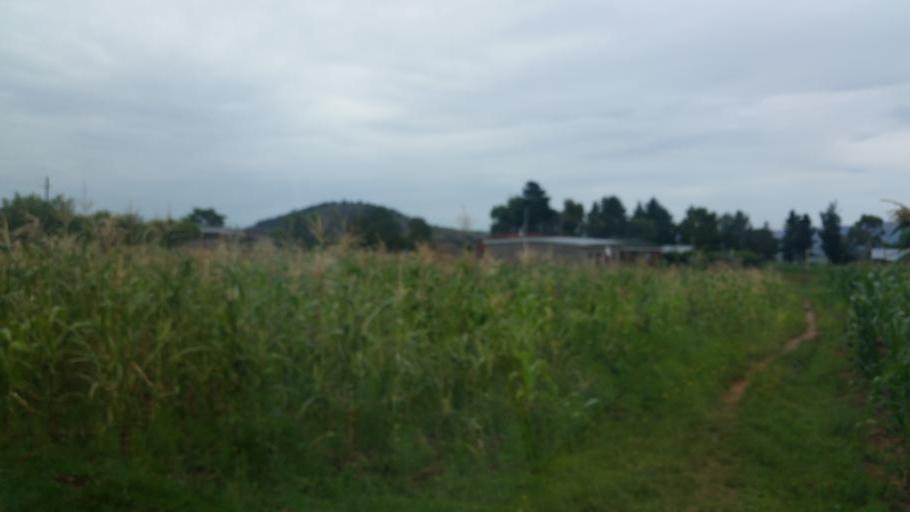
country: LS
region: Berea
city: Teyateyaneng
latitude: -29.1176
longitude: 27.9611
